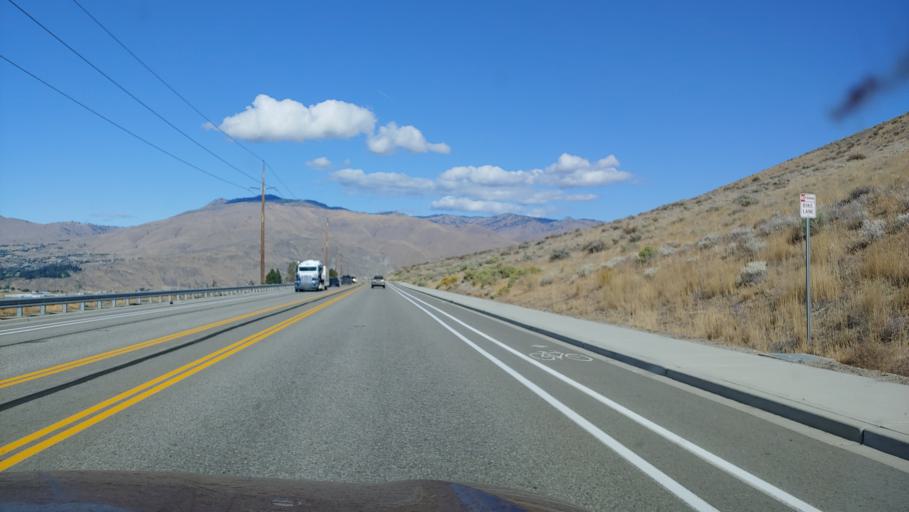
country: US
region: Washington
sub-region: Douglas County
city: East Wenatchee Bench
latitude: 47.4484
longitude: -120.2870
